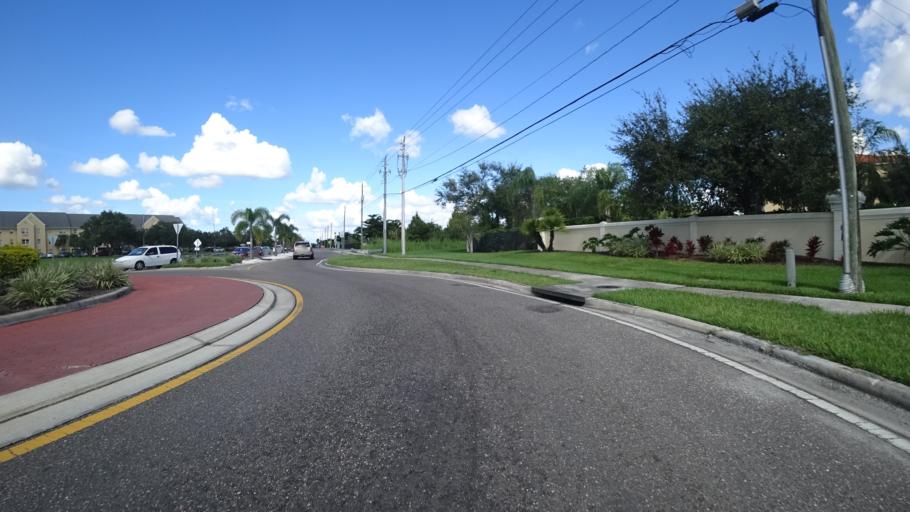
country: US
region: Florida
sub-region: Manatee County
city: Palmetto
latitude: 27.5160
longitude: -82.5525
